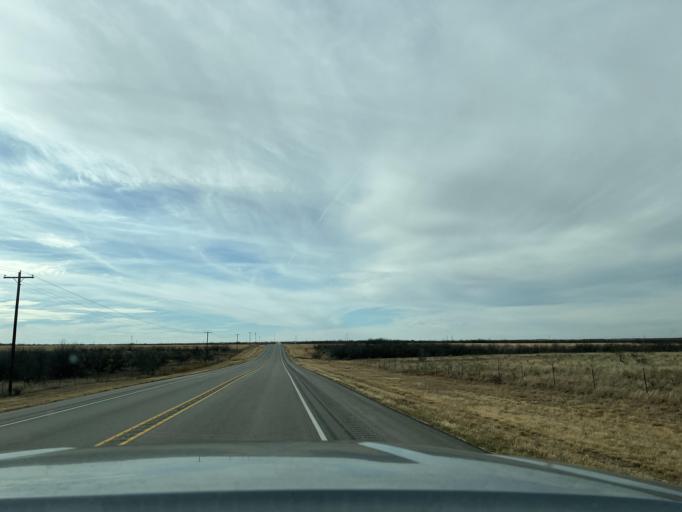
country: US
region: Texas
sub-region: Jones County
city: Anson
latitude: 32.7506
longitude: -99.6836
